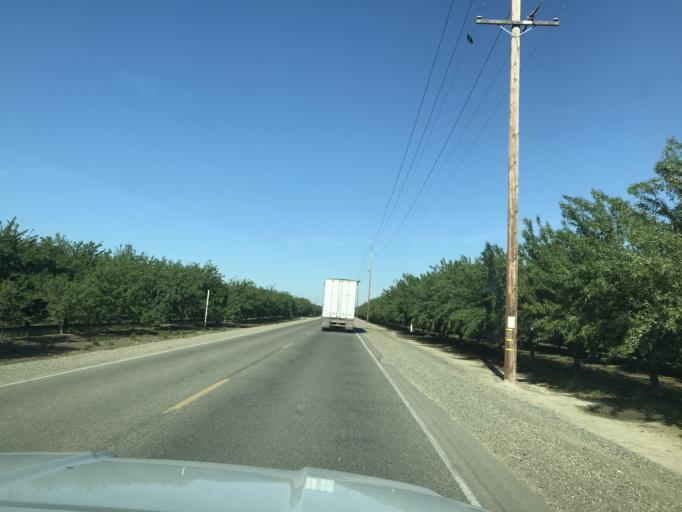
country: US
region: California
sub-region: Fresno County
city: Kerman
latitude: 36.6619
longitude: -120.1102
